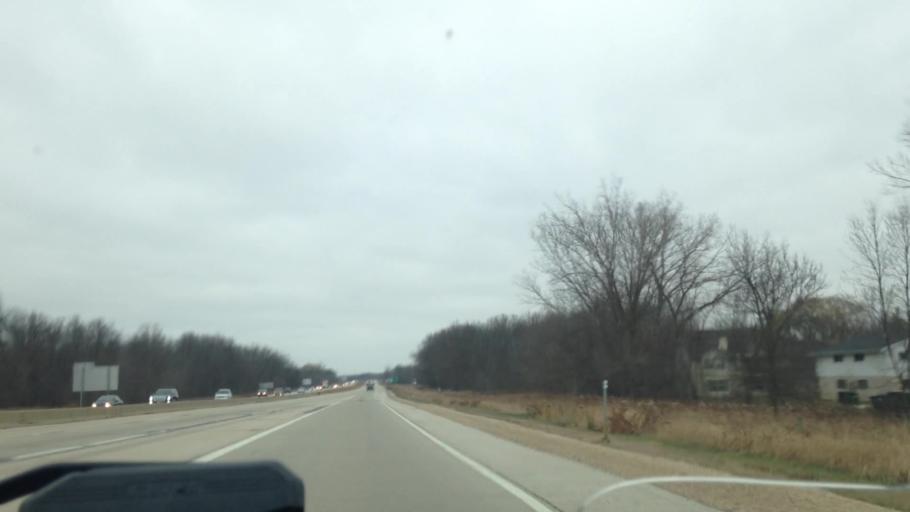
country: US
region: Wisconsin
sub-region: Washington County
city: Slinger
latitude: 43.4198
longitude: -88.3341
